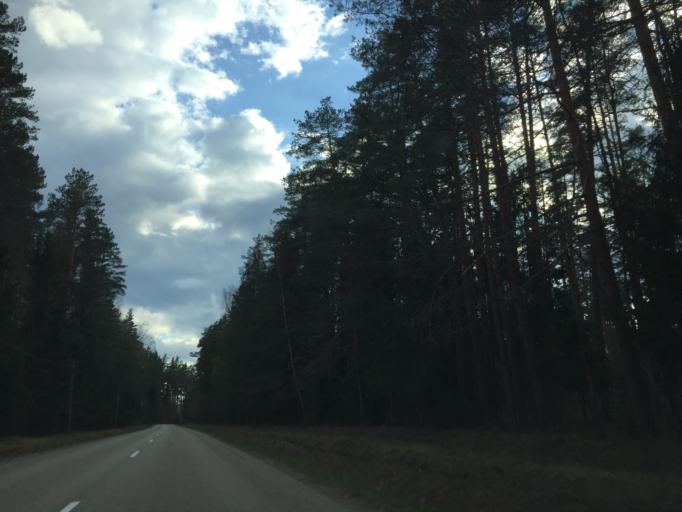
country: LV
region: Priekuli
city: Priekuli
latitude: 57.3726
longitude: 25.4074
